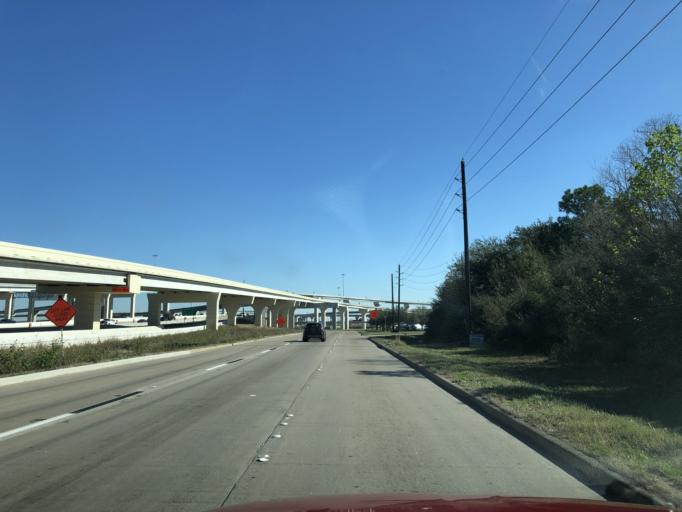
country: US
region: Texas
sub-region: Brazoria County
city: Brookside Village
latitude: 29.5965
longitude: -95.3935
